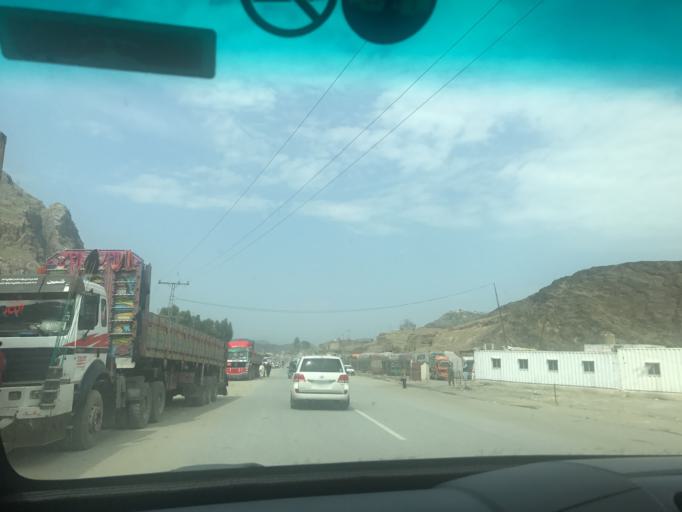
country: PK
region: Federally Administered Tribal Areas
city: Landi Kotal
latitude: 34.1174
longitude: 71.1008
